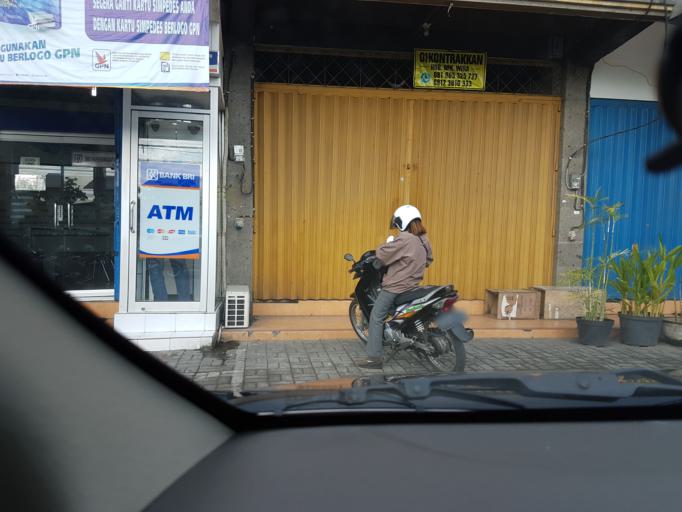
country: ID
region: Bali
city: Denpasar
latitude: -8.6698
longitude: 115.1909
